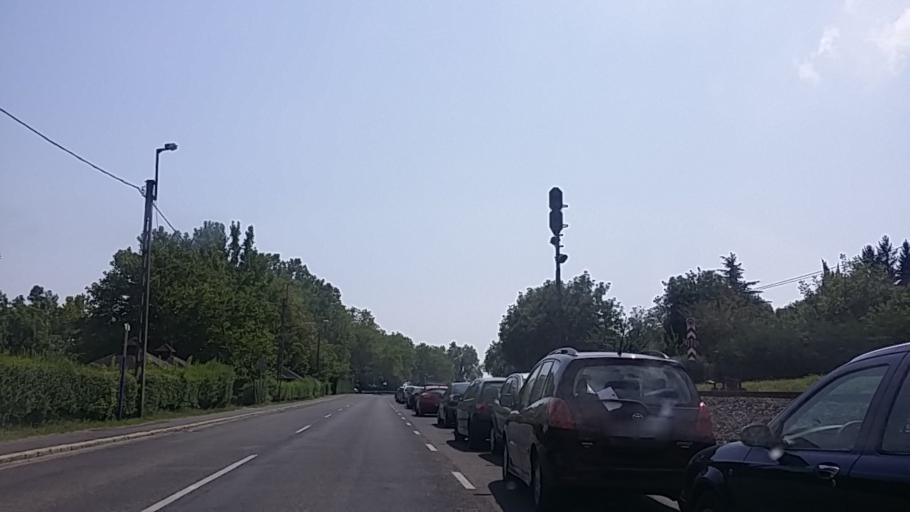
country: HU
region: Veszprem
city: Badacsonytomaj
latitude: 46.7991
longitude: 17.5161
